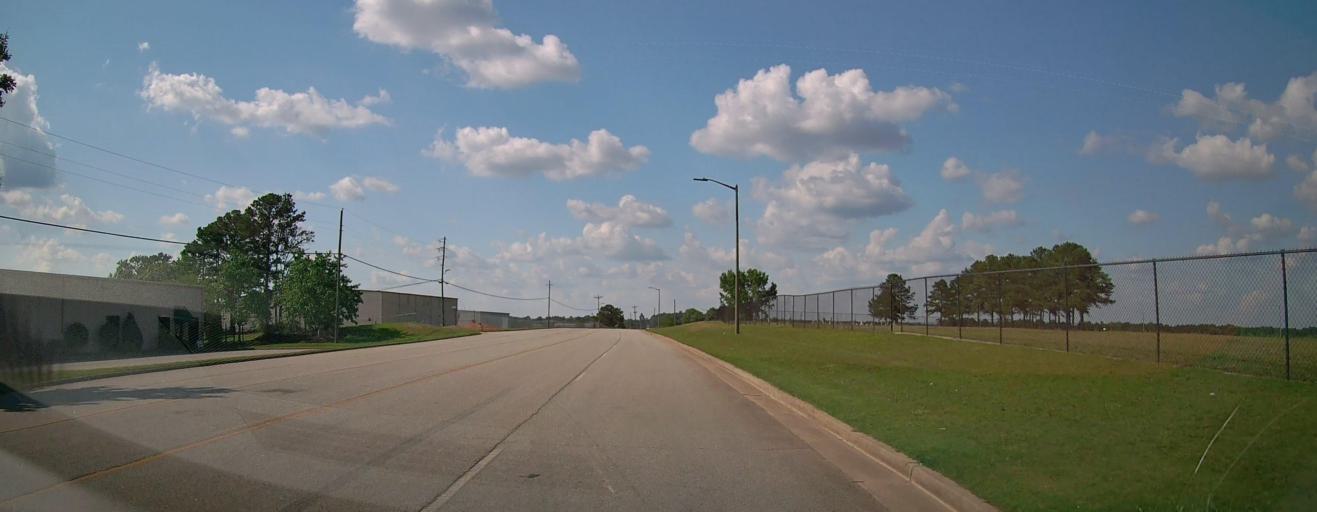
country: US
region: Georgia
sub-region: Henry County
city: Hampton
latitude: 33.3843
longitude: -84.3248
